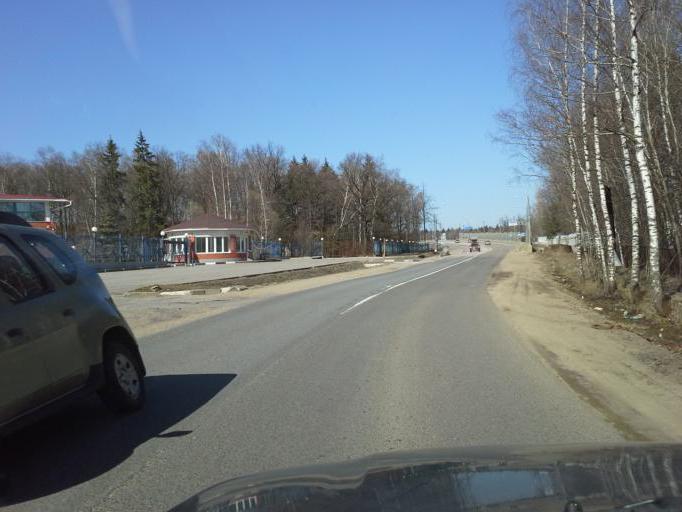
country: RU
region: Moskovskaya
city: Kokoshkino
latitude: 55.6185
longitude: 37.1547
